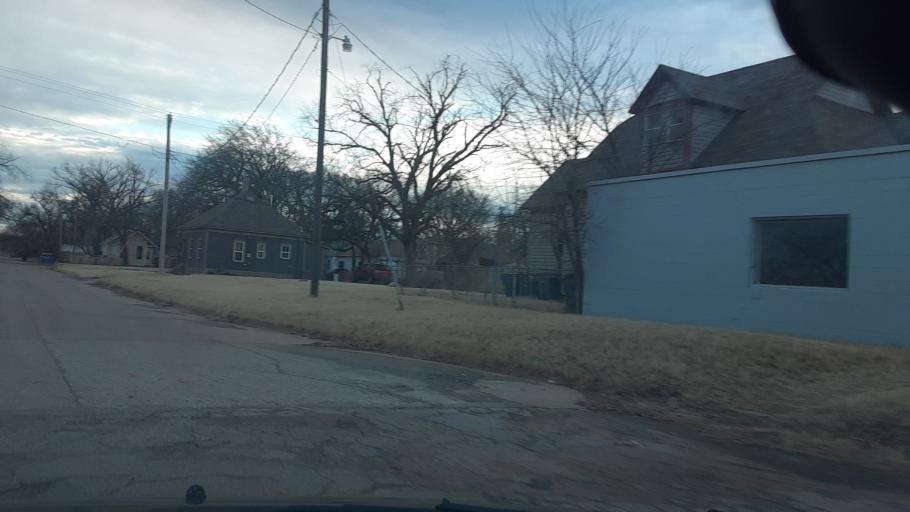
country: US
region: Oklahoma
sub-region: Logan County
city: Guthrie
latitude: 35.8739
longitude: -97.4254
